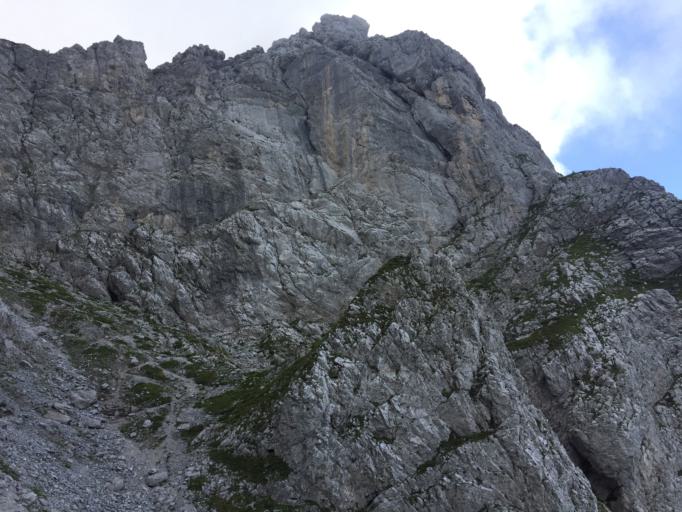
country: IT
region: Friuli Venezia Giulia
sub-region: Provincia di Udine
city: Forni Avoltri
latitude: 46.5516
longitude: 12.7690
